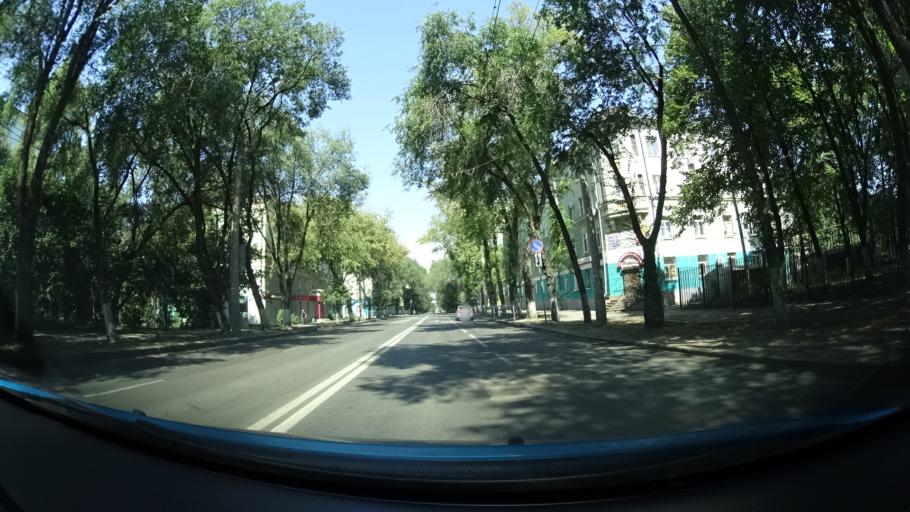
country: RU
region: Samara
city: Samara
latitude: 53.2079
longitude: 50.1597
